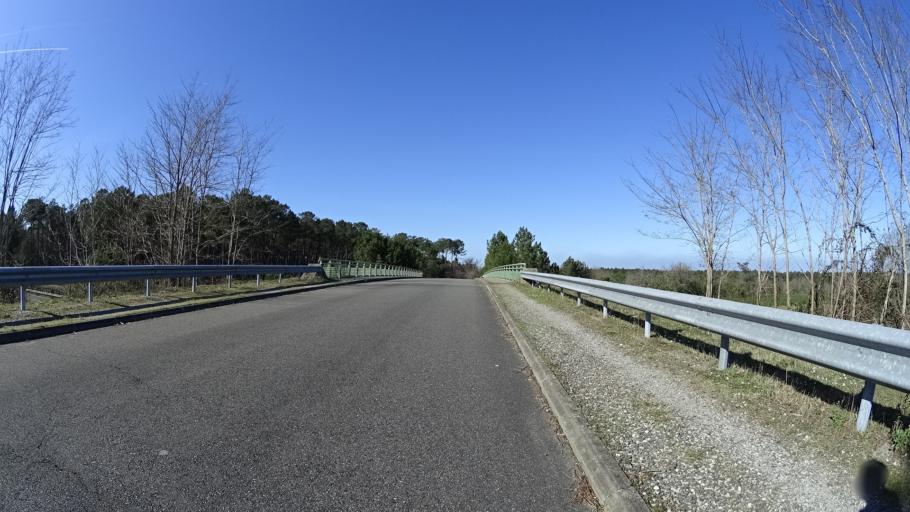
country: FR
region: Aquitaine
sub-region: Departement des Landes
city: Mees
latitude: 43.7379
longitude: -1.0959
